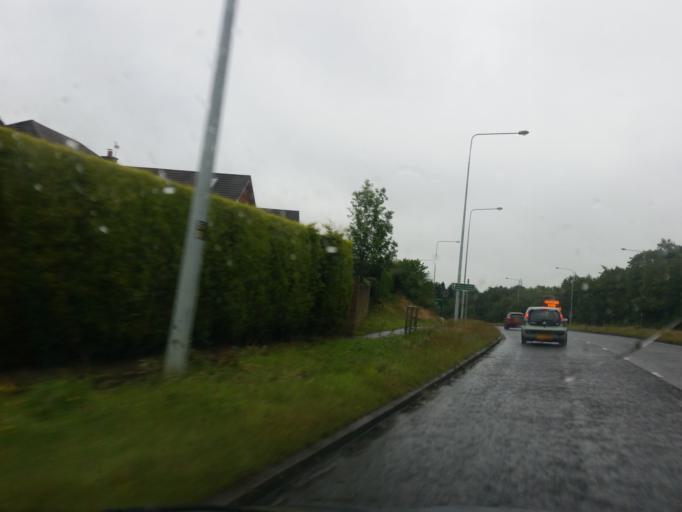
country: GB
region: Northern Ireland
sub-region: North Down District
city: Bangor
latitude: 54.6456
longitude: -5.6808
